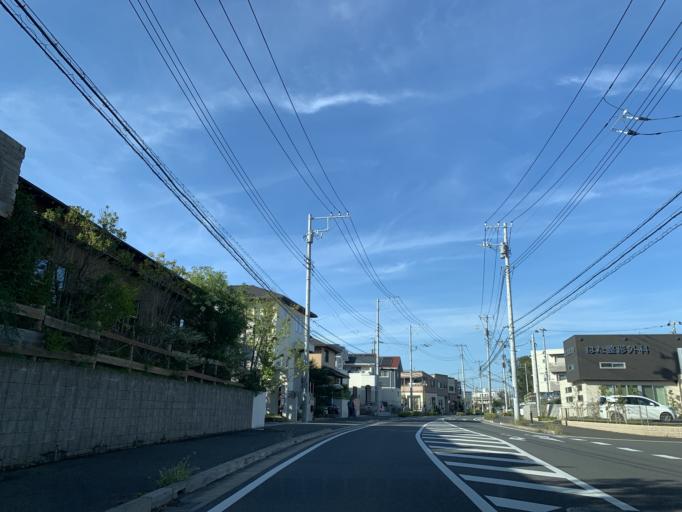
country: JP
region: Chiba
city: Nagareyama
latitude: 35.8772
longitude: 139.9269
